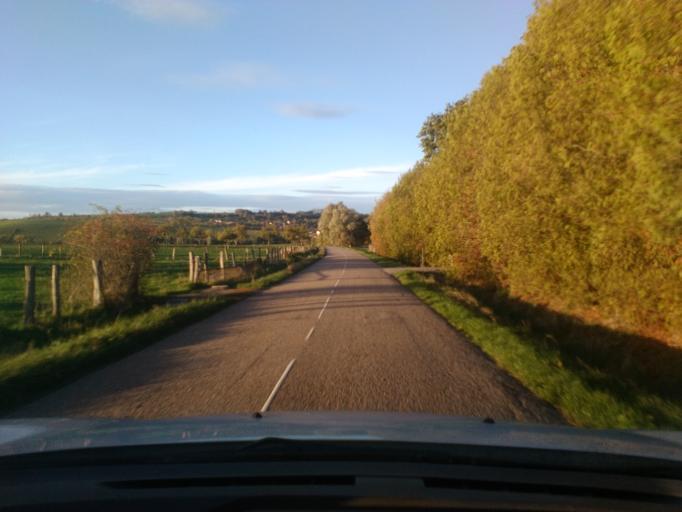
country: FR
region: Lorraine
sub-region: Departement des Vosges
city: Charmes
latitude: 48.3519
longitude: 6.2553
